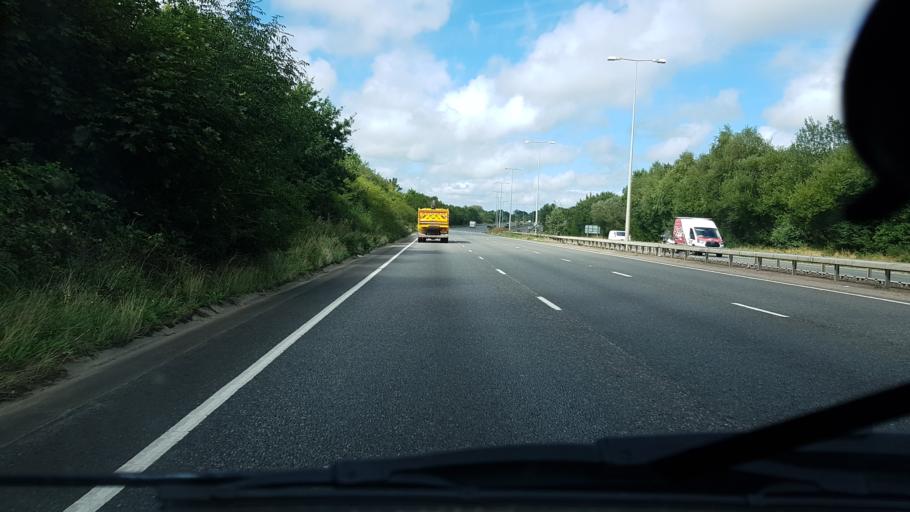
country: GB
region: England
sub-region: West Sussex
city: Broadfield
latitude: 51.0652
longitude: -0.2044
